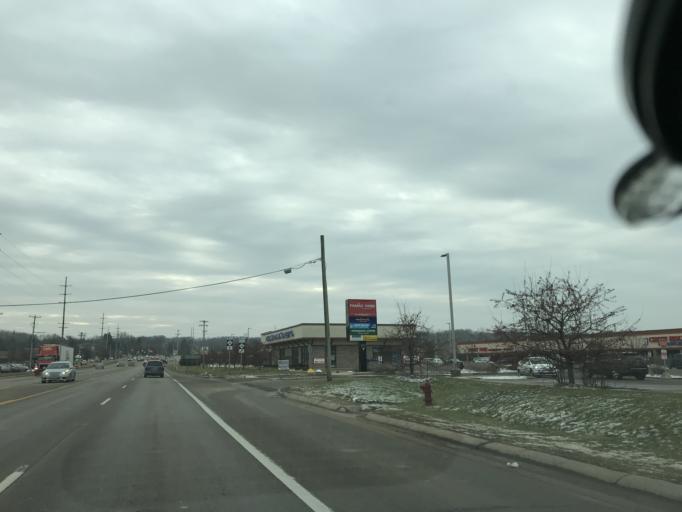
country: US
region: Michigan
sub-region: Kent County
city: Northview
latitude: 43.0590
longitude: -85.5800
